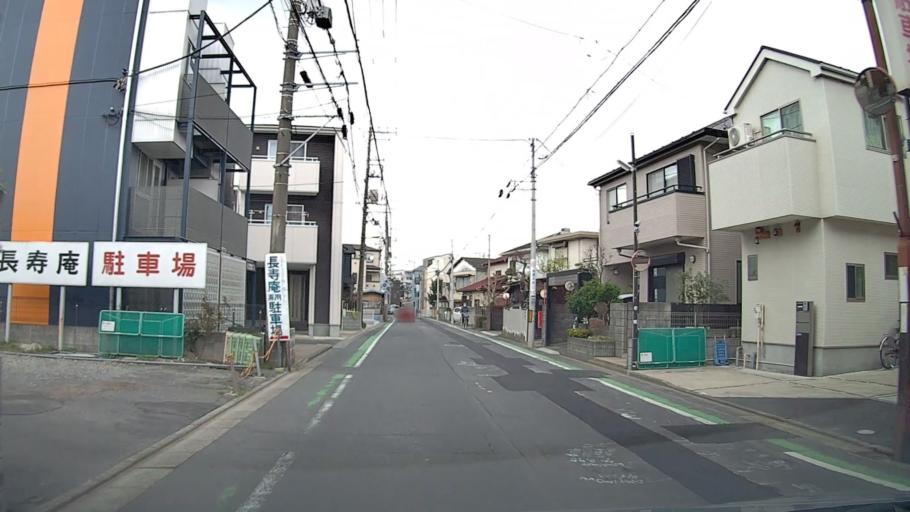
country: JP
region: Saitama
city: Asaka
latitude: 35.8008
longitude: 139.5970
